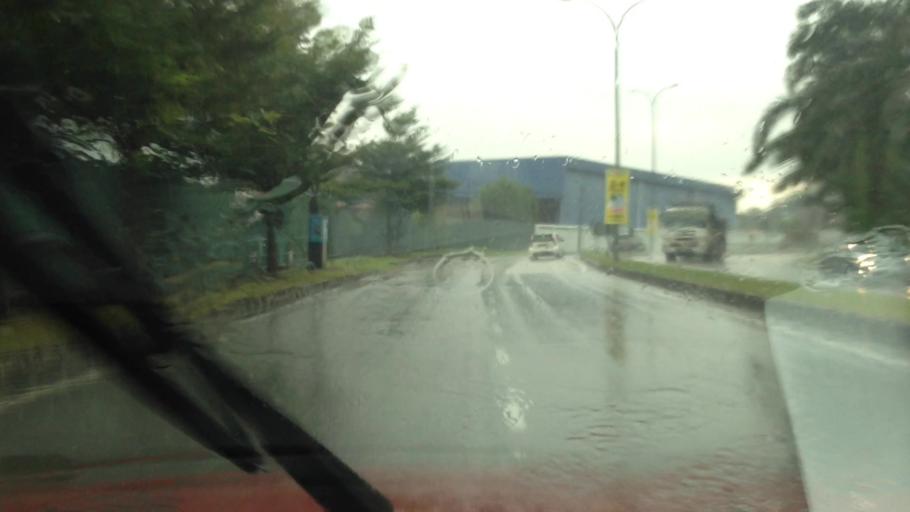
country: MY
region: Selangor
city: Subang Jaya
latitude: 3.0271
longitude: 101.5893
